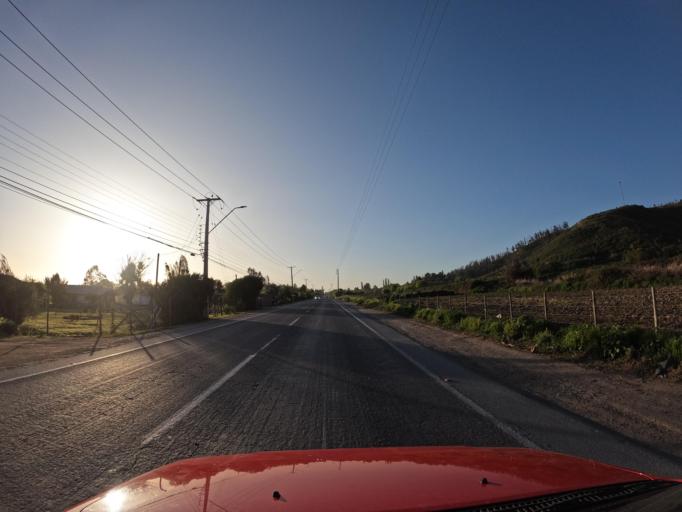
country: CL
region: O'Higgins
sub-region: Provincia de Cachapoal
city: San Vicente
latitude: -34.2673
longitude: -71.3693
